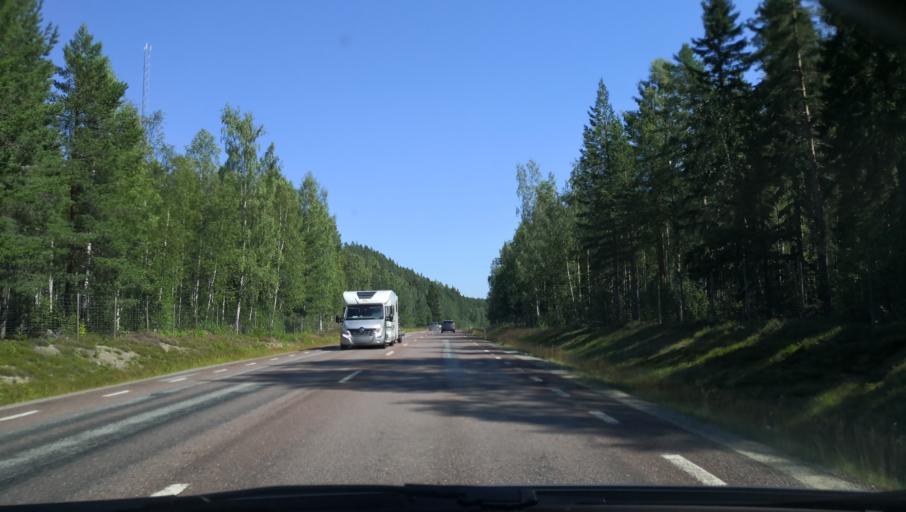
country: SE
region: Gaevleborg
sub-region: Ovanakers Kommun
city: Alfta
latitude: 61.3440
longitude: 16.1084
